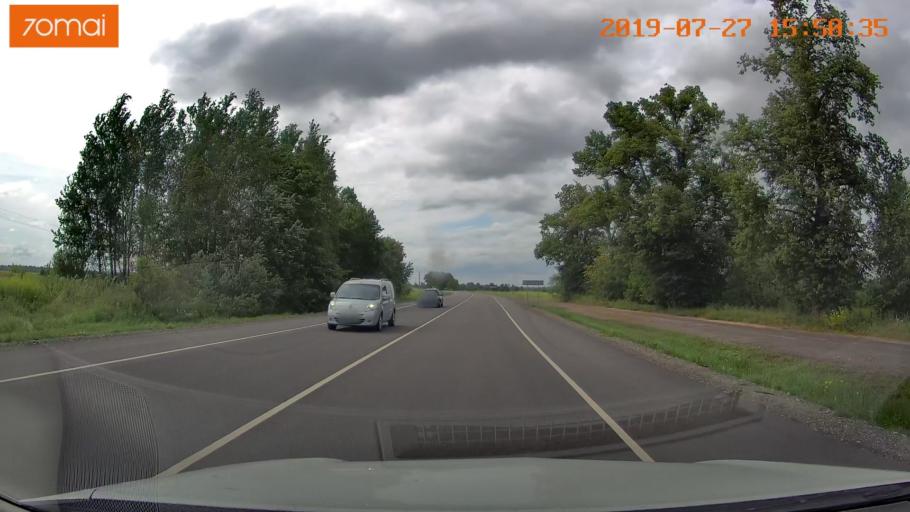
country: RU
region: Kaliningrad
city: Chernyakhovsk
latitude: 54.6012
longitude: 22.0034
